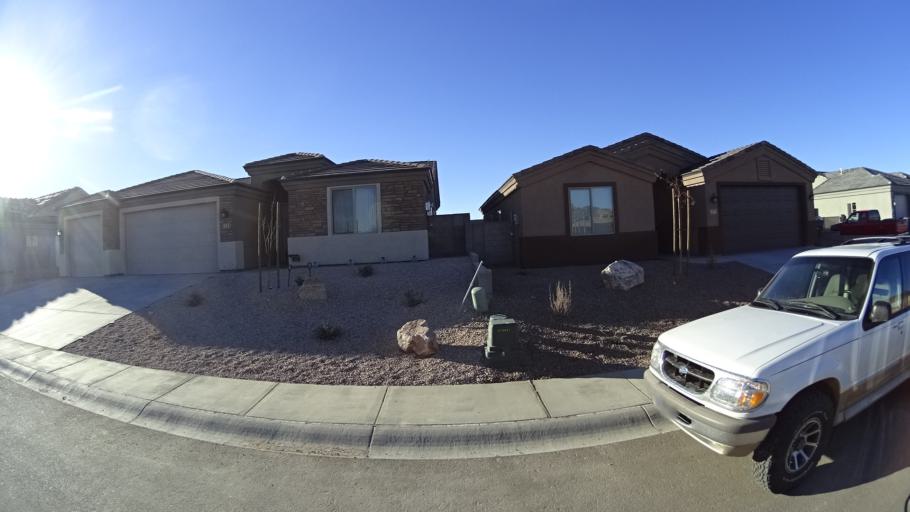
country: US
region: Arizona
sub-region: Mohave County
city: Kingman
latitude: 35.1908
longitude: -113.9988
